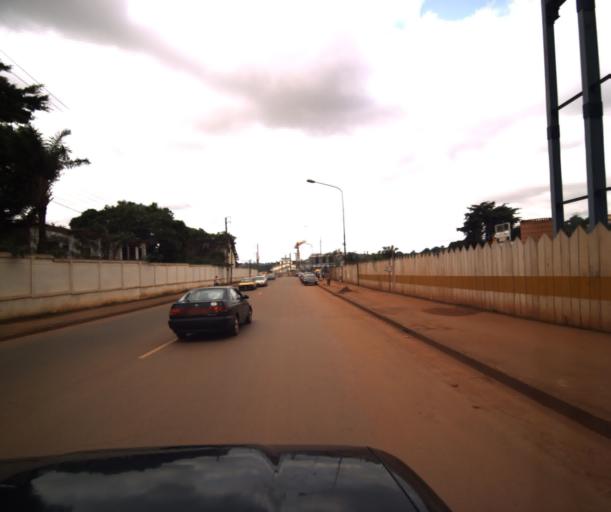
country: CM
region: Centre
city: Yaounde
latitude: 3.8434
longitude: 11.5160
